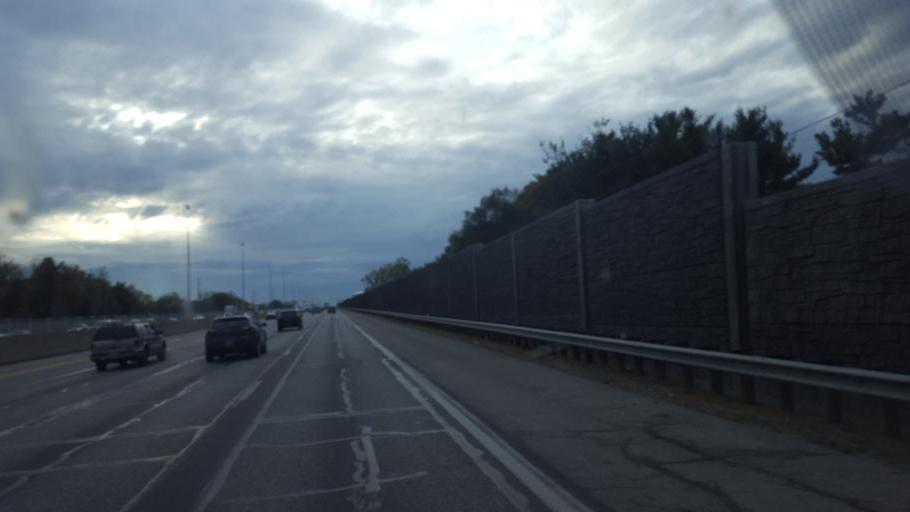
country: US
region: Ohio
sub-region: Franklin County
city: Worthington
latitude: 40.1122
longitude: -83.0471
